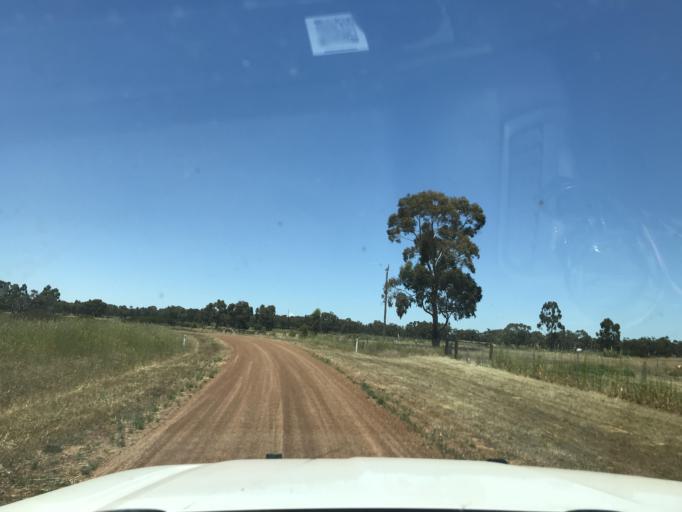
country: AU
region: South Australia
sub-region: Wattle Range
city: Penola
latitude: -37.0440
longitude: 141.3817
